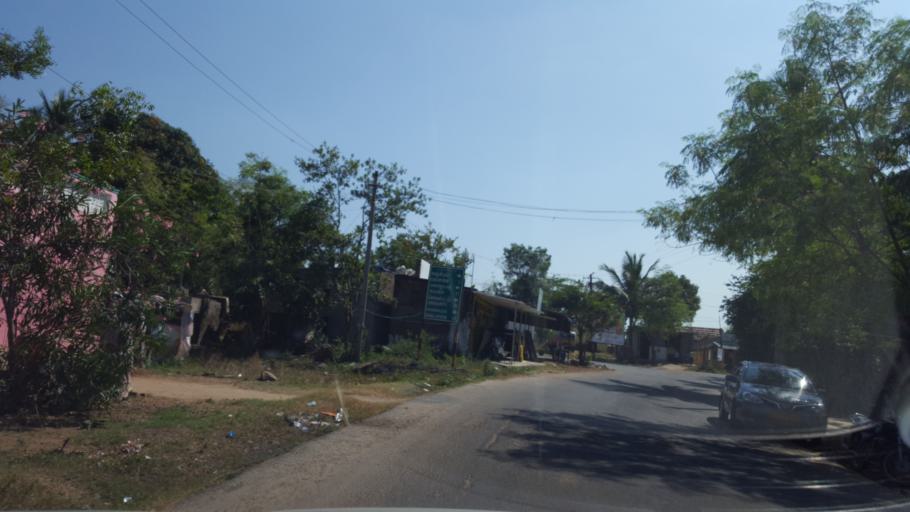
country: IN
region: Tamil Nadu
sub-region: Kancheepuram
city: Kanchipuram
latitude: 12.8366
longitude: 79.7393
